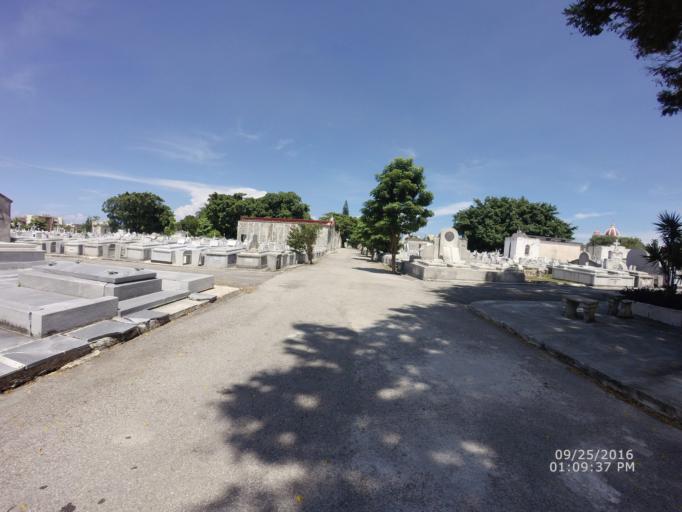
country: CU
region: La Habana
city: Havana
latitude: 23.1217
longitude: -82.4007
